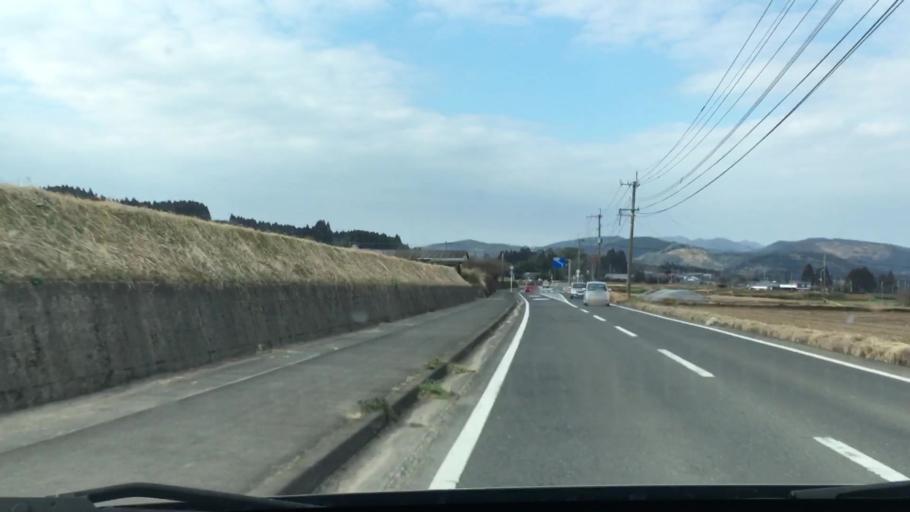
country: JP
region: Miyazaki
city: Kushima
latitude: 31.5175
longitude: 131.2387
